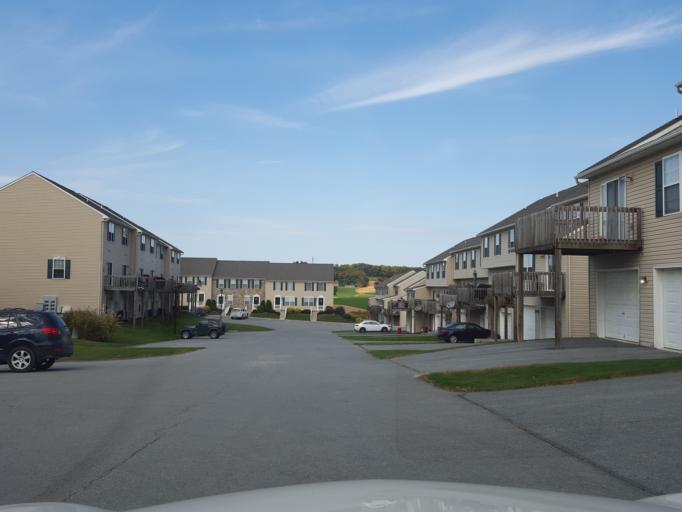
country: US
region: Pennsylvania
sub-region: York County
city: Yoe
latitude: 39.9201
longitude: -76.6257
